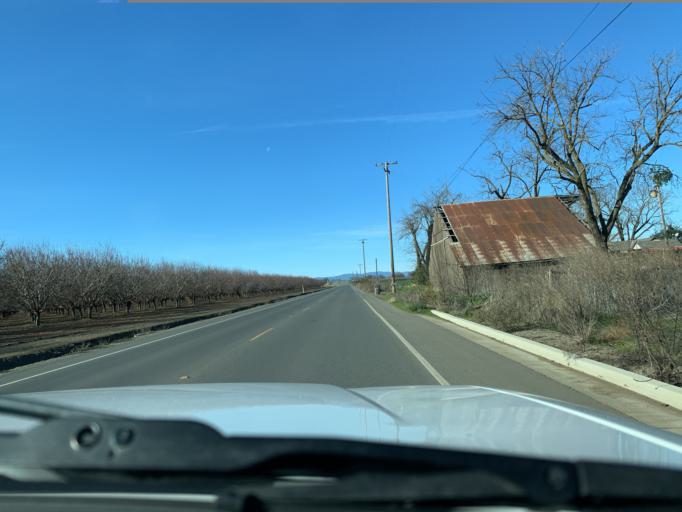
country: US
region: California
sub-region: Yolo County
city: Woodland
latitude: 38.6410
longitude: -121.7505
